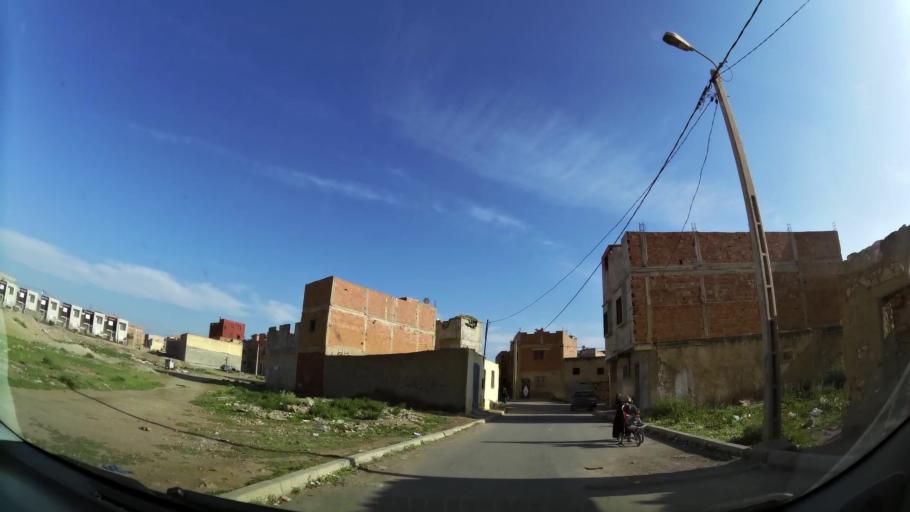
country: MA
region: Oriental
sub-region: Oujda-Angad
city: Oujda
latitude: 34.7157
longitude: -1.8971
